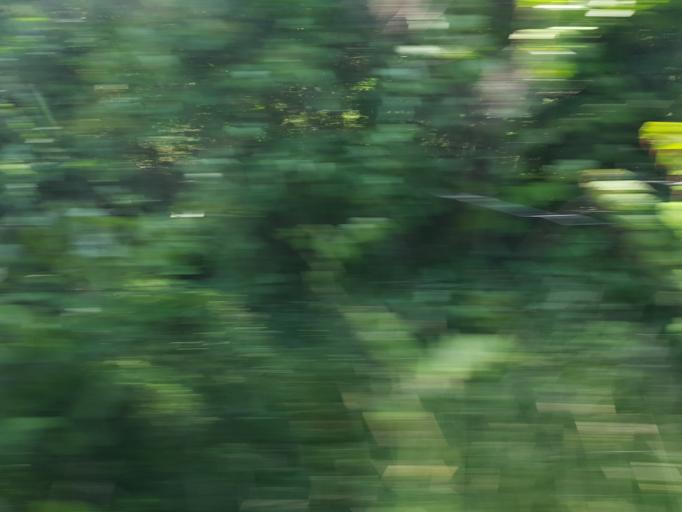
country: SE
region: Vaestra Goetaland
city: Ronnang
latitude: 57.9542
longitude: 11.6200
